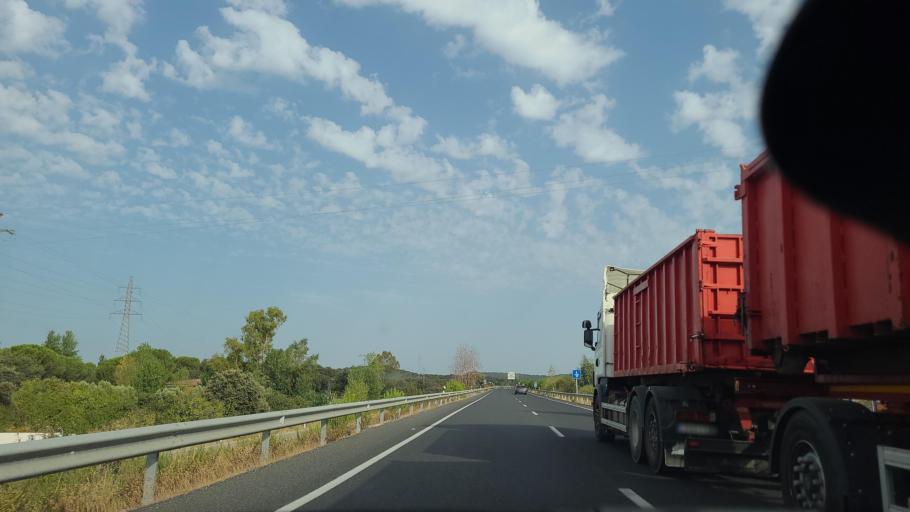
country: ES
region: Andalusia
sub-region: Province of Cordoba
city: Villaharta
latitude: 38.0907
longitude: -4.8646
